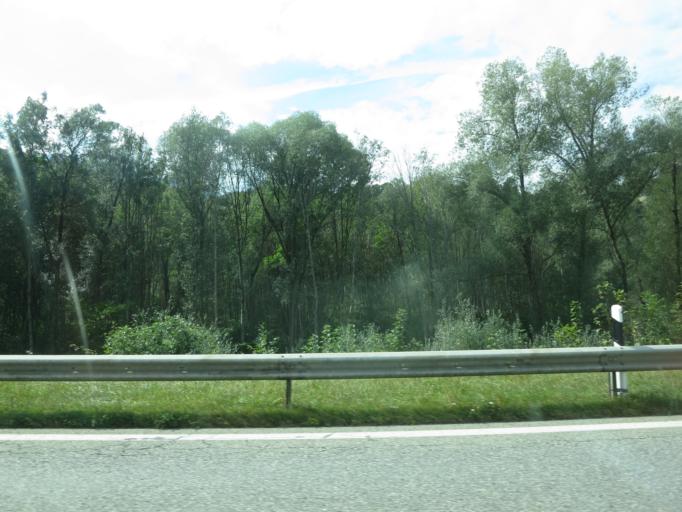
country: CH
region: Grisons
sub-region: Imboden District
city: Bonaduz
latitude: 46.8141
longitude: 9.4076
